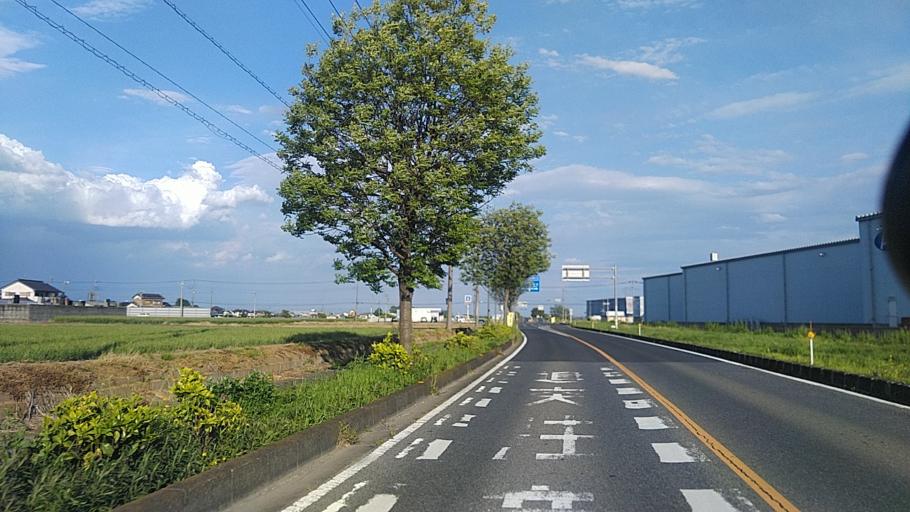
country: JP
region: Gunma
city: Tatebayashi
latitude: 36.2217
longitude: 139.5837
